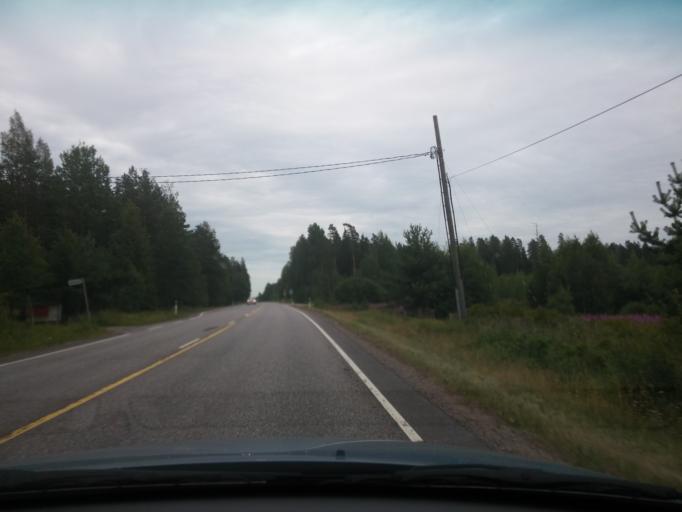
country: FI
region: Haeme
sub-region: Riihimaeki
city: Loppi
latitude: 60.7255
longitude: 24.4117
